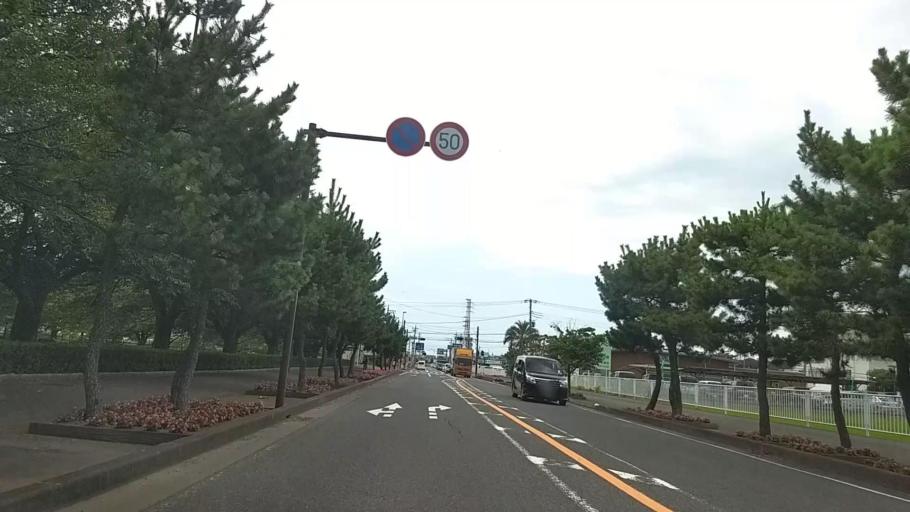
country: JP
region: Kanagawa
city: Chigasaki
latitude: 35.3745
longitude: 139.3837
